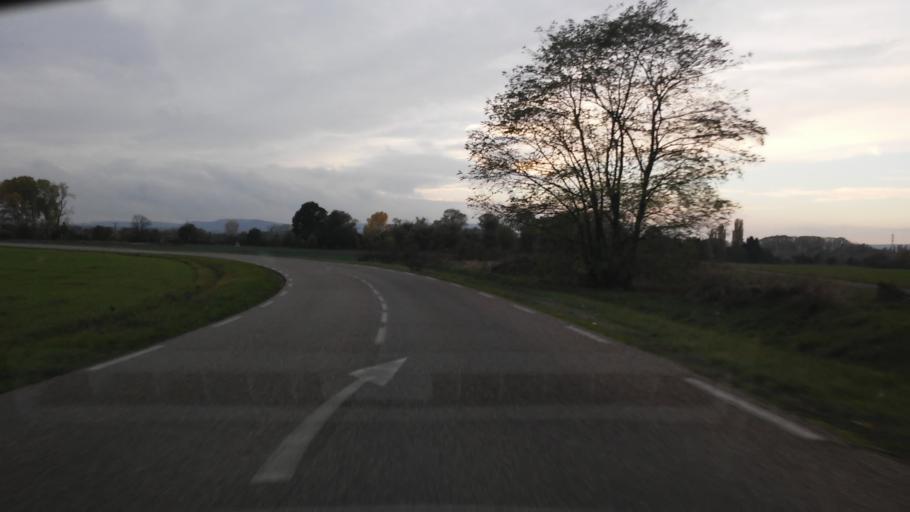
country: FR
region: Lorraine
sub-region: Departement de la Moselle
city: Ay-sur-Moselle
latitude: 49.2449
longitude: 6.1992
